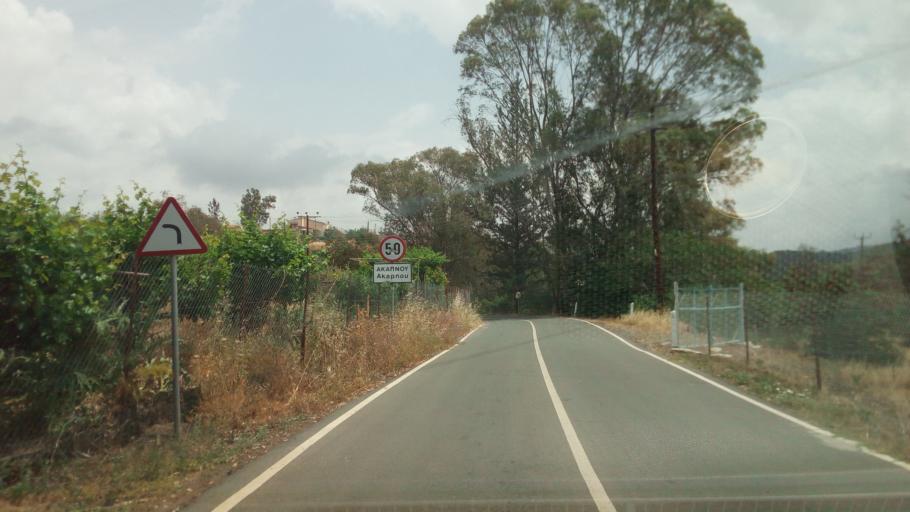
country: CY
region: Limassol
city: Parekklisha
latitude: 34.8385
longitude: 33.1839
